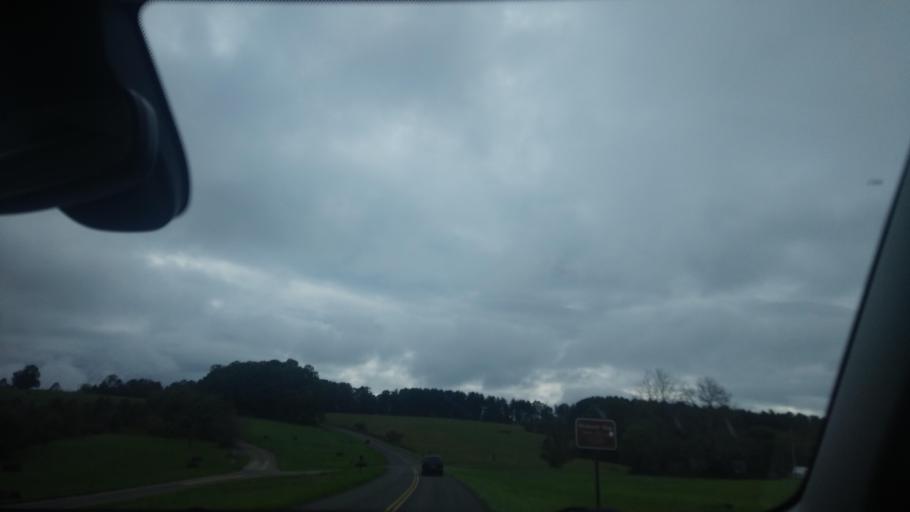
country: US
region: Virginia
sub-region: Carroll County
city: Cana
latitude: 36.6634
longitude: -80.6037
